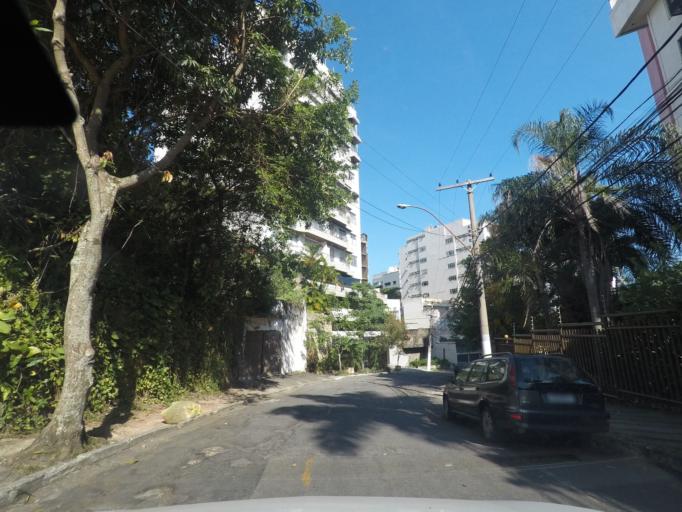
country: BR
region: Rio de Janeiro
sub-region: Niteroi
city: Niteroi
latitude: -22.9074
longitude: -43.1309
